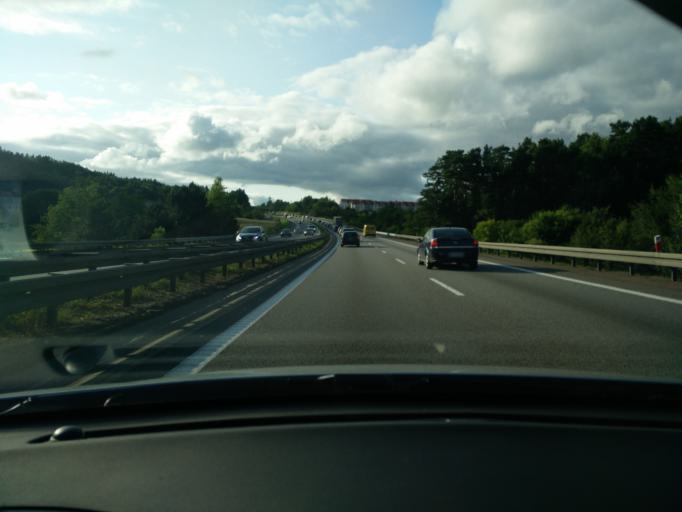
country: PL
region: Pomeranian Voivodeship
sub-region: Gdynia
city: Wielki Kack
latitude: 54.4588
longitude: 18.4889
